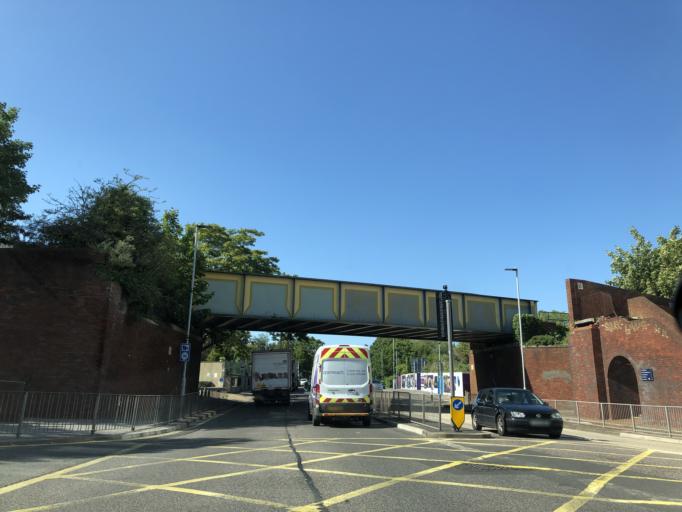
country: GB
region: England
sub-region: Portsmouth
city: Portsmouth
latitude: 50.7970
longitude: -1.0958
